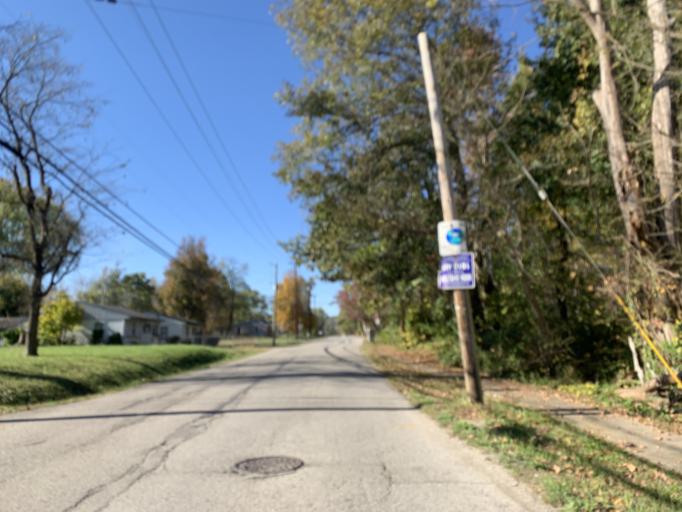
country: US
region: Kentucky
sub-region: Jefferson County
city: Saint Dennis
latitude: 38.1908
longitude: -85.8701
